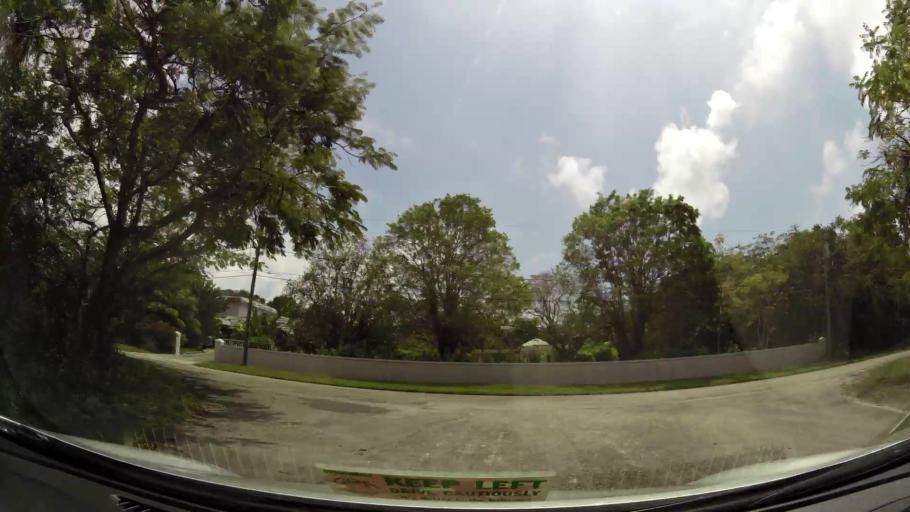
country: BS
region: Freeport
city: Lucaya
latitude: 26.5198
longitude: -78.6468
